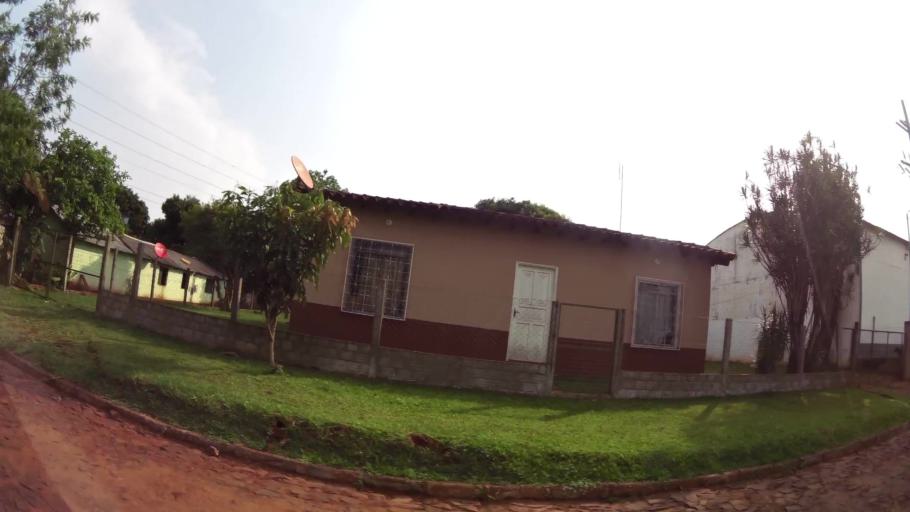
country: PY
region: Alto Parana
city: Ciudad del Este
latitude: -25.4670
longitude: -54.6372
